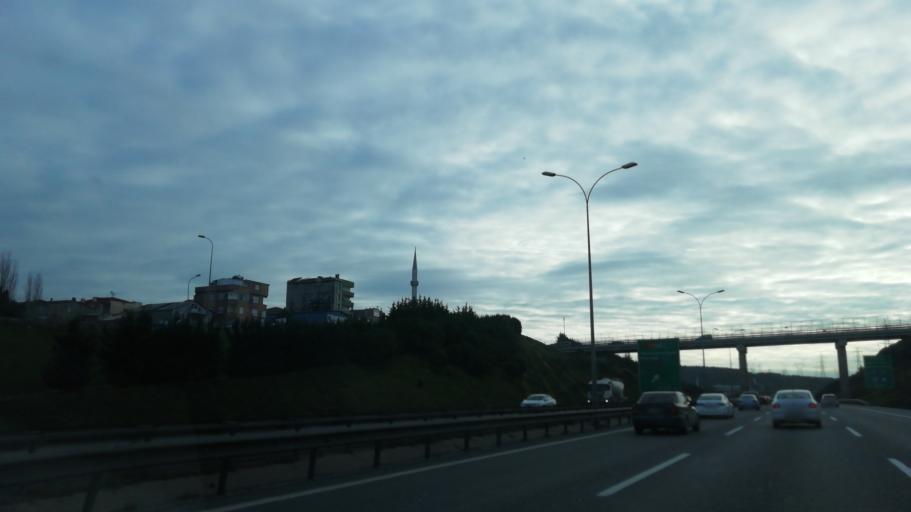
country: TR
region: Istanbul
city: Sultanbeyli
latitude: 40.9530
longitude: 29.2985
